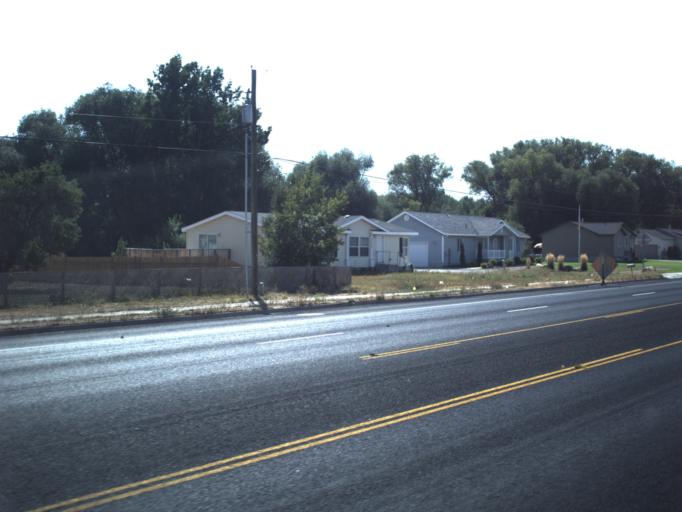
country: US
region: Utah
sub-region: Cache County
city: Nibley
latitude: 41.6843
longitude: -111.8339
